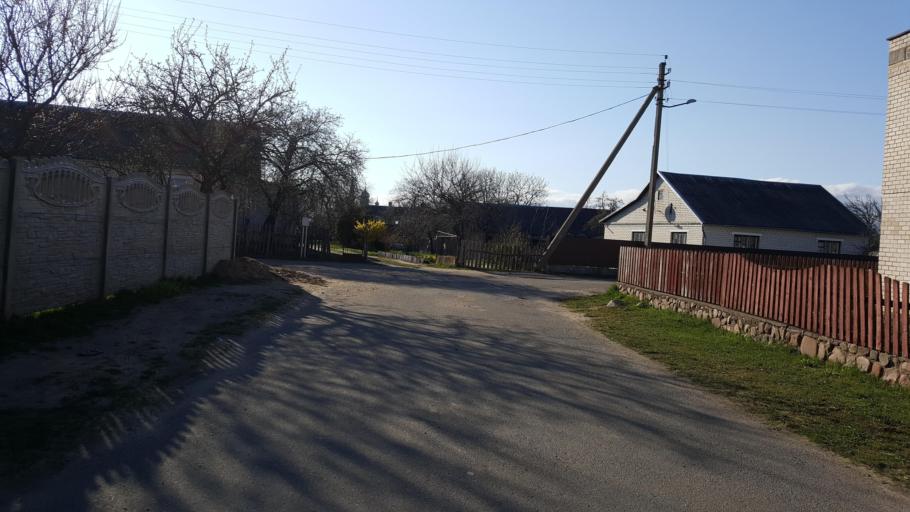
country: BY
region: Brest
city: Kamyanyets
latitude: 52.4022
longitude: 23.8299
